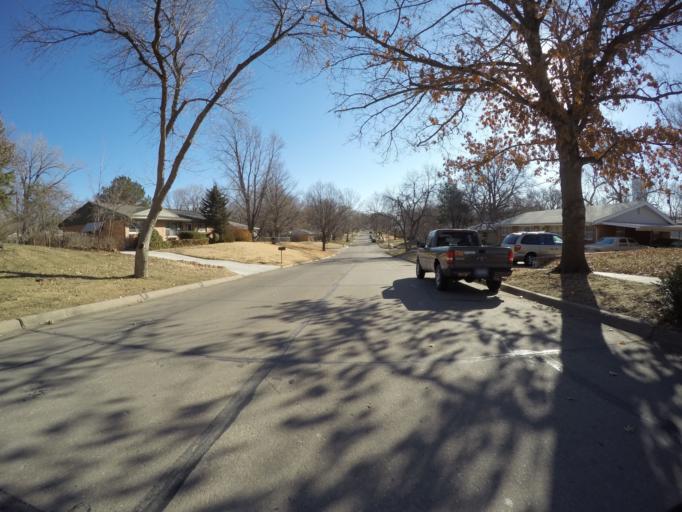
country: US
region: Kansas
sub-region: Riley County
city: Manhattan
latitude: 39.1987
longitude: -96.6041
